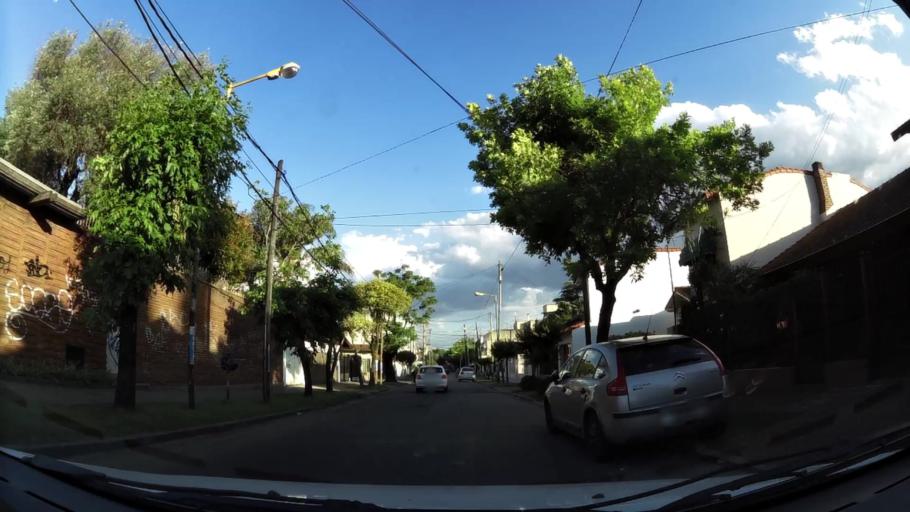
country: AR
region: Buenos Aires
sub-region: Partido de General San Martin
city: General San Martin
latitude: -34.5577
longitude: -58.5553
